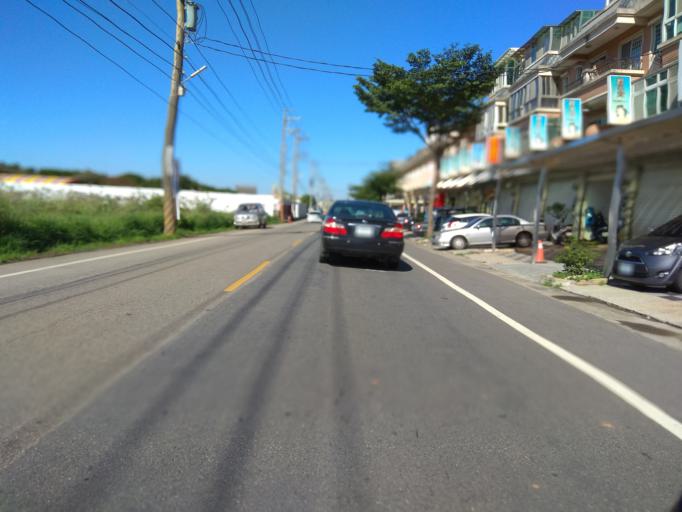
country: TW
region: Taiwan
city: Taoyuan City
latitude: 24.9684
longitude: 121.1466
